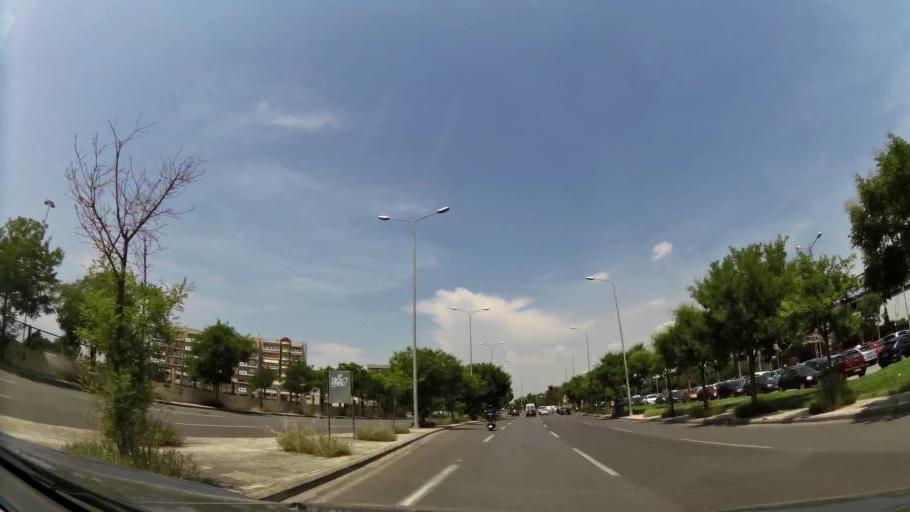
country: GR
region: Central Macedonia
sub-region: Nomos Thessalonikis
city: Ampelokipoi
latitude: 40.6447
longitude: 22.9197
